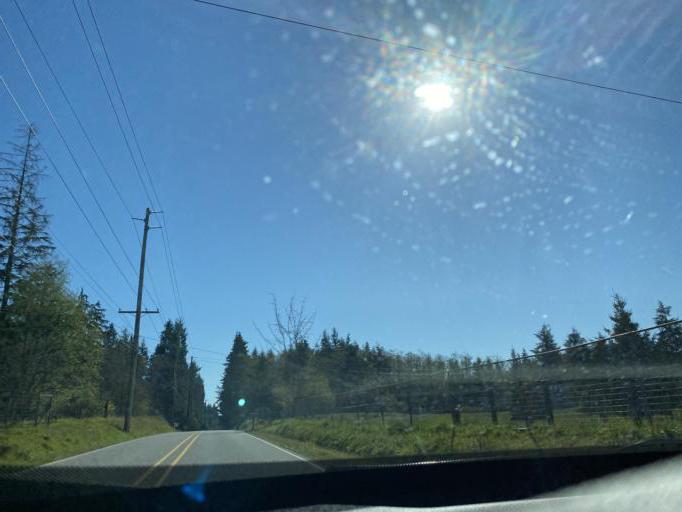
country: US
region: Washington
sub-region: Island County
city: Freeland
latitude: 48.0798
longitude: -122.5963
